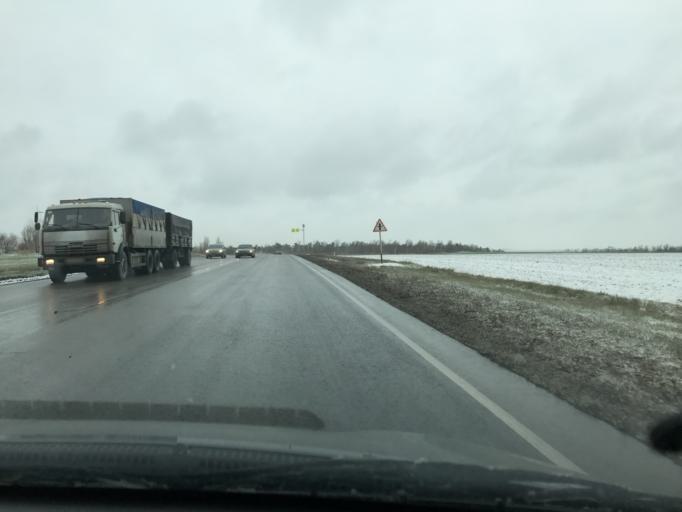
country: RU
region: Rostov
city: Kagal'nitskaya
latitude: 46.8948
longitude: 40.1279
